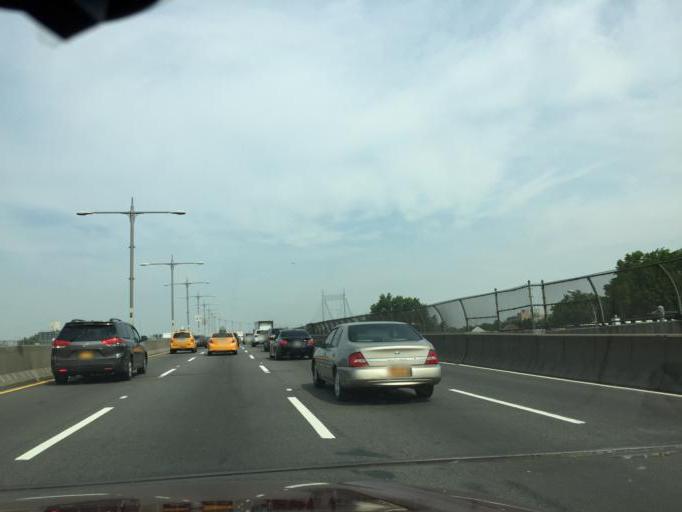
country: US
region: New York
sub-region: Queens County
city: Long Island City
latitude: 40.7723
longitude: -73.9197
